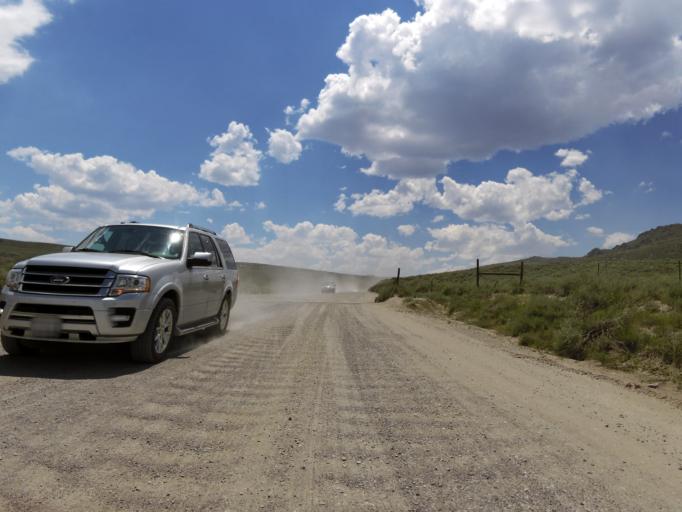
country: US
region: California
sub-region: Mono County
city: Bridgeport
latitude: 38.2031
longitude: -119.0207
